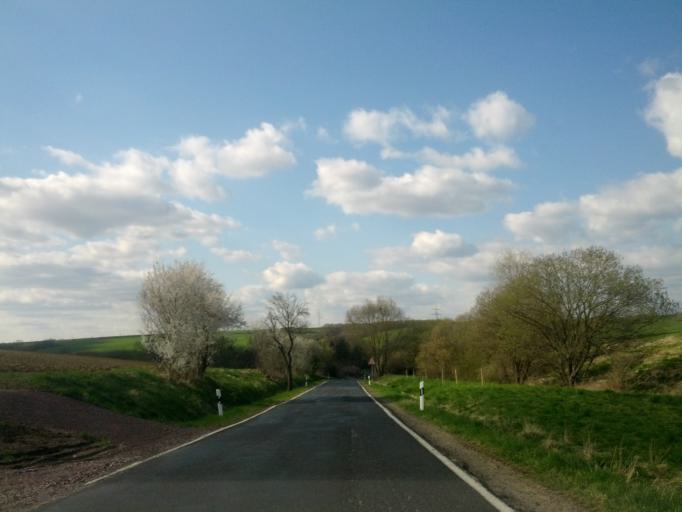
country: DE
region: Thuringia
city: Haina
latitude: 50.9693
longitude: 10.4775
